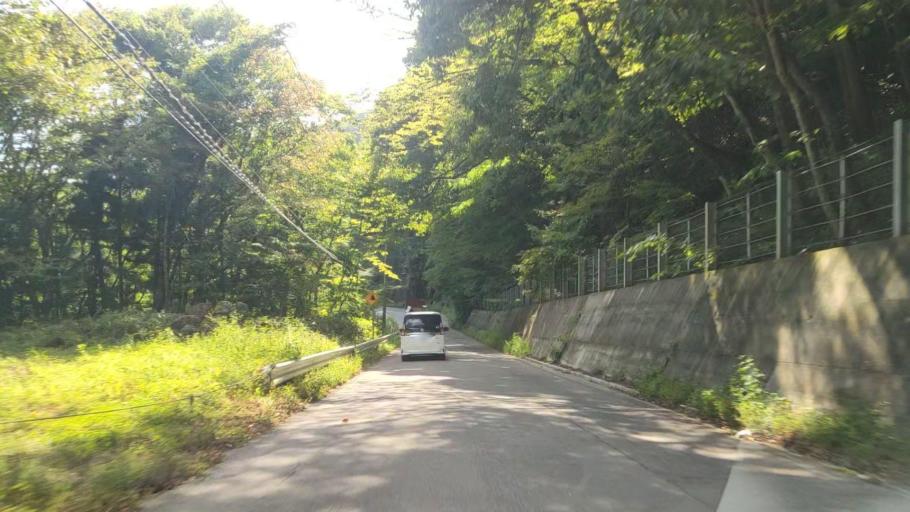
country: JP
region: Gunma
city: Nakanojomachi
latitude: 36.6327
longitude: 138.6526
